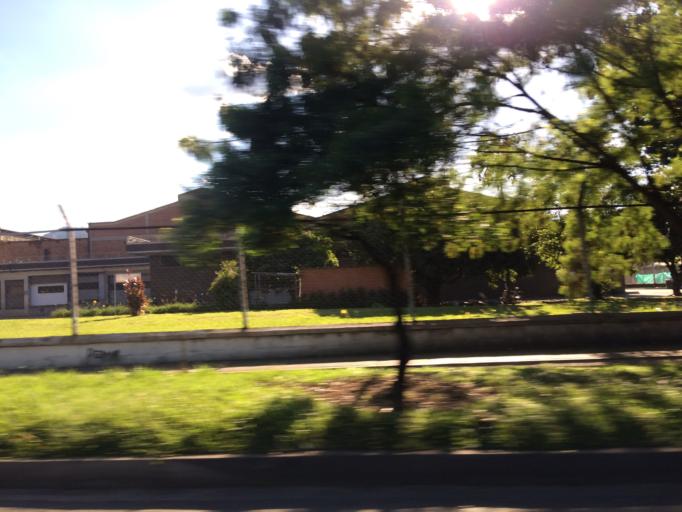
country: CO
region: Antioquia
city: Itagui
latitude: 6.2071
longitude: -75.5794
